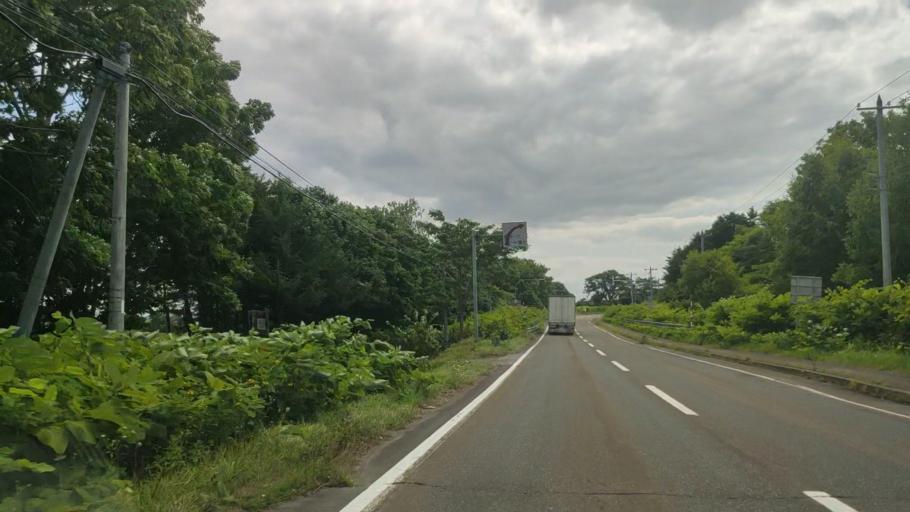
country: JP
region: Hokkaido
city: Rumoi
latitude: 44.5611
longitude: 141.7858
